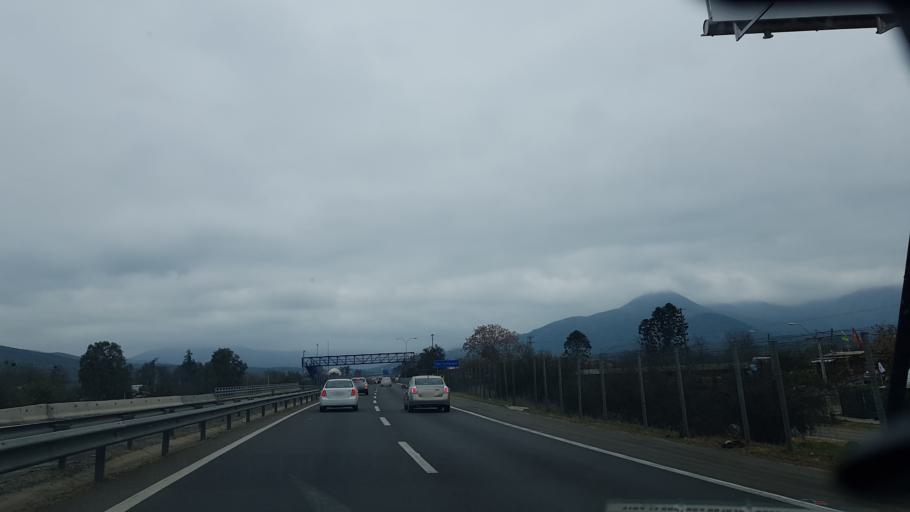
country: CL
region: Santiago Metropolitan
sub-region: Provincia de Melipilla
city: Melipilla
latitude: -33.4132
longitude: -71.1526
